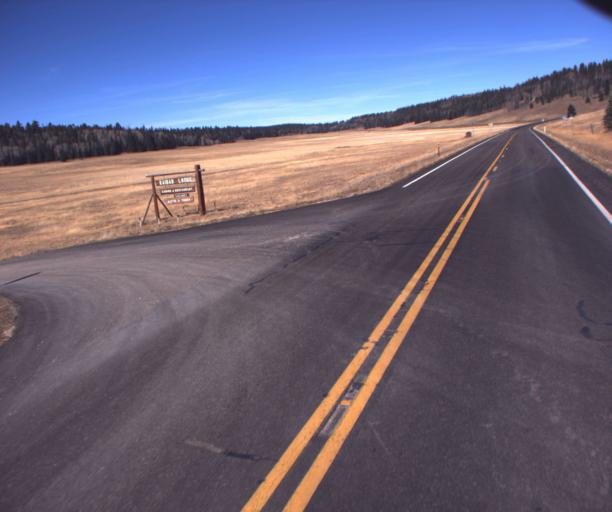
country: US
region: Arizona
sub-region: Coconino County
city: Grand Canyon
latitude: 36.4140
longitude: -112.1310
